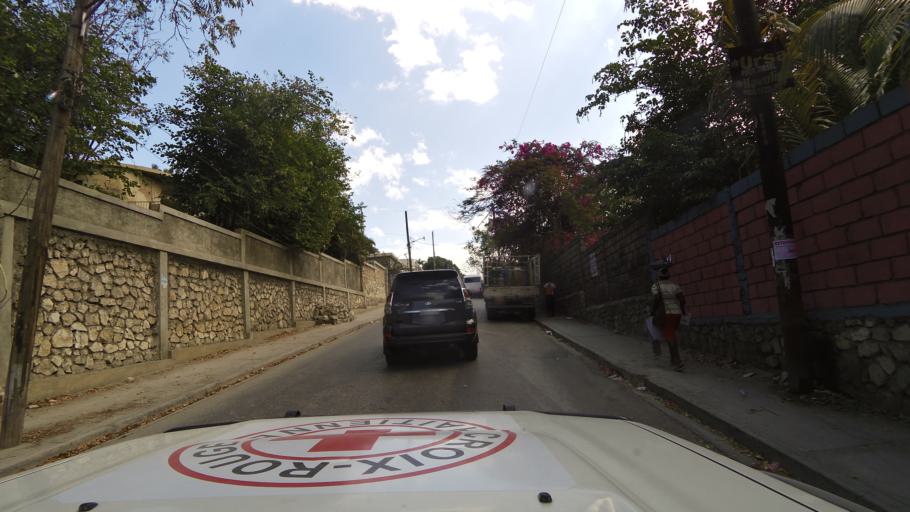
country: HT
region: Ouest
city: Delmas 73
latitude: 18.5303
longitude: -72.2936
